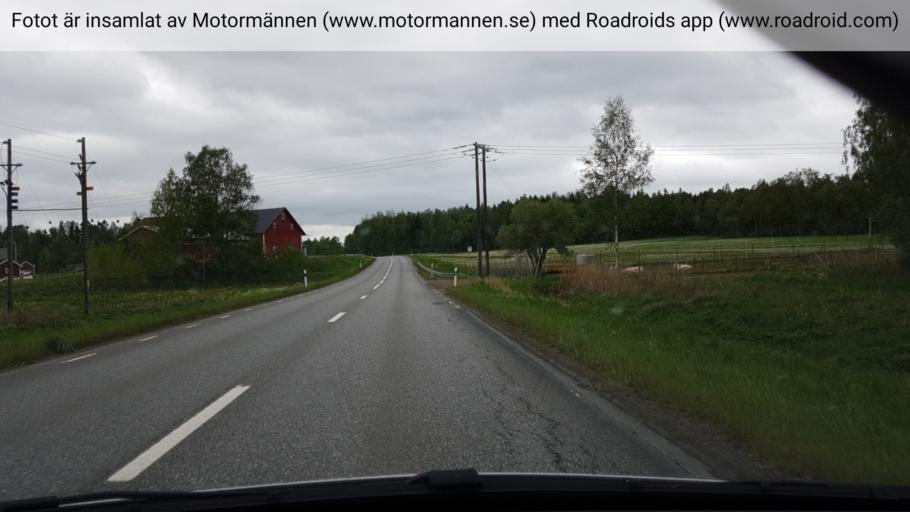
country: SE
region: Joenkoeping
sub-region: Aneby Kommun
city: Aneby
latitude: 57.9798
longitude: 14.8219
